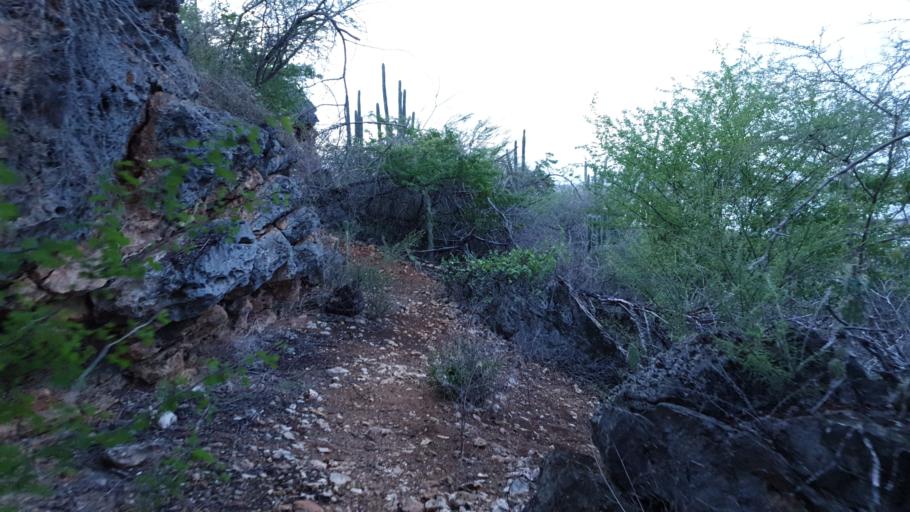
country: CW
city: Newport
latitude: 12.1313
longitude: -68.8151
